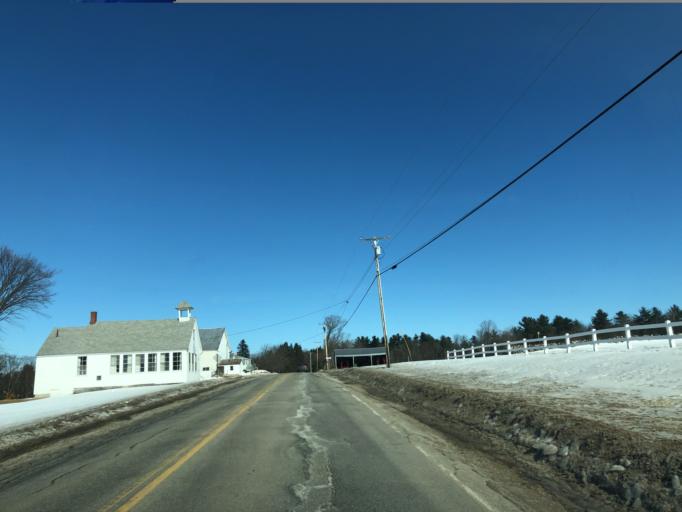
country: US
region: Maine
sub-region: Oxford County
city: Hebron
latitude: 44.2053
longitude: -70.3457
